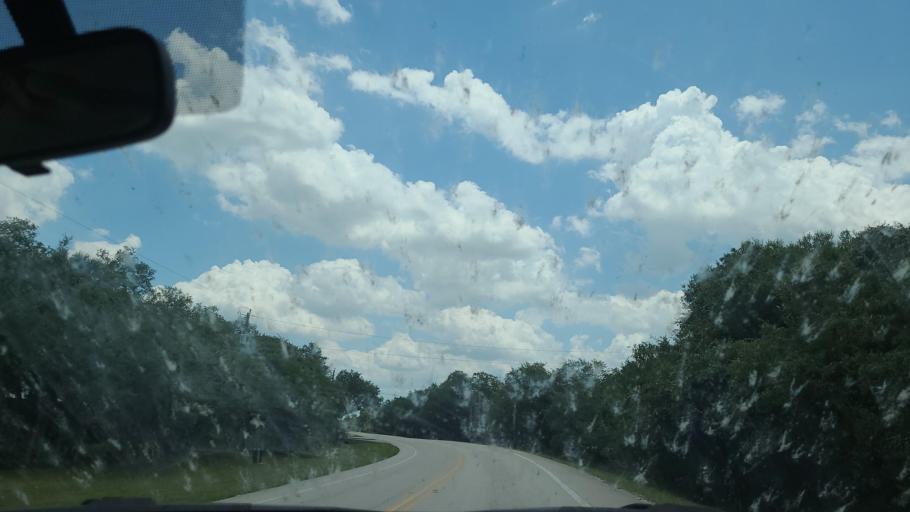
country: US
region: Florida
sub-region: Glades County
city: Buckhead Ridge
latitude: 27.1182
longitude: -81.0782
